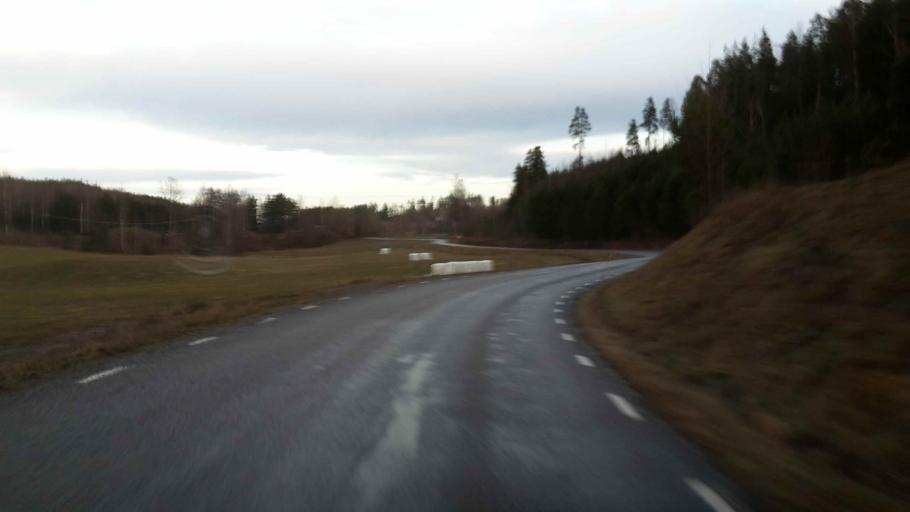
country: SE
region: Kalmar
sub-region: Vasterviks Kommun
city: Overum
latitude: 58.1614
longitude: 16.3317
